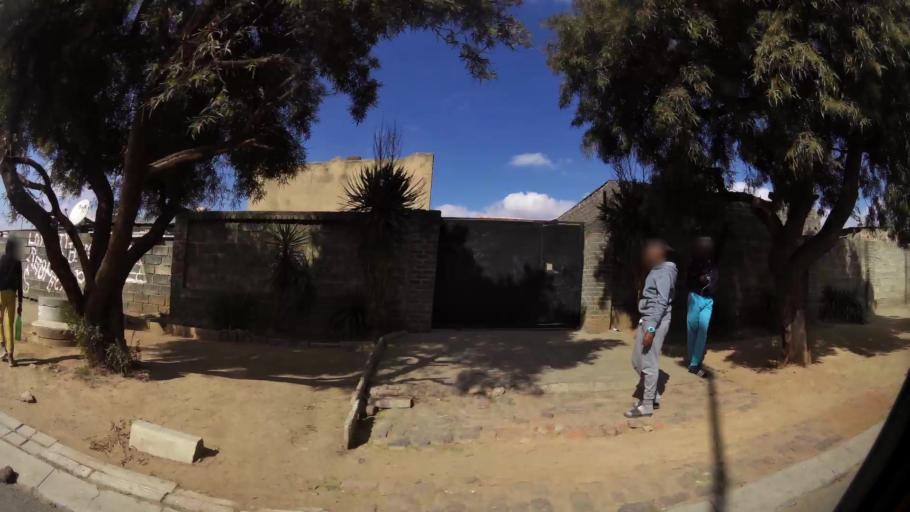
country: ZA
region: Gauteng
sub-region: Ekurhuleni Metropolitan Municipality
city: Tembisa
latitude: -26.0175
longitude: 28.1929
